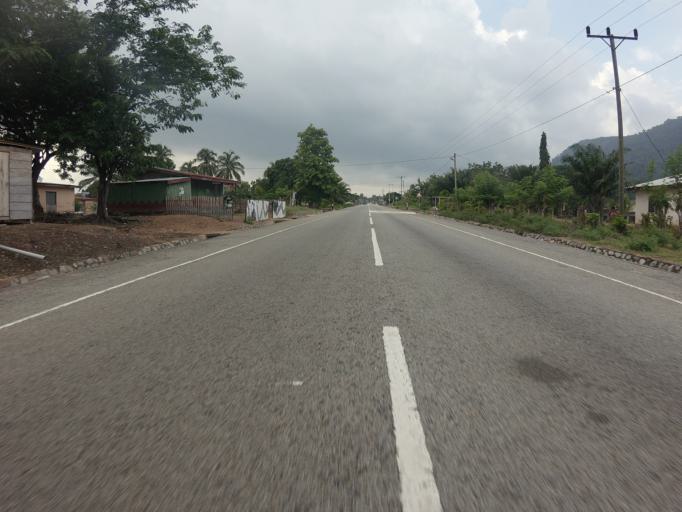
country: GH
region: Volta
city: Ho
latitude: 6.7654
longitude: 0.4803
